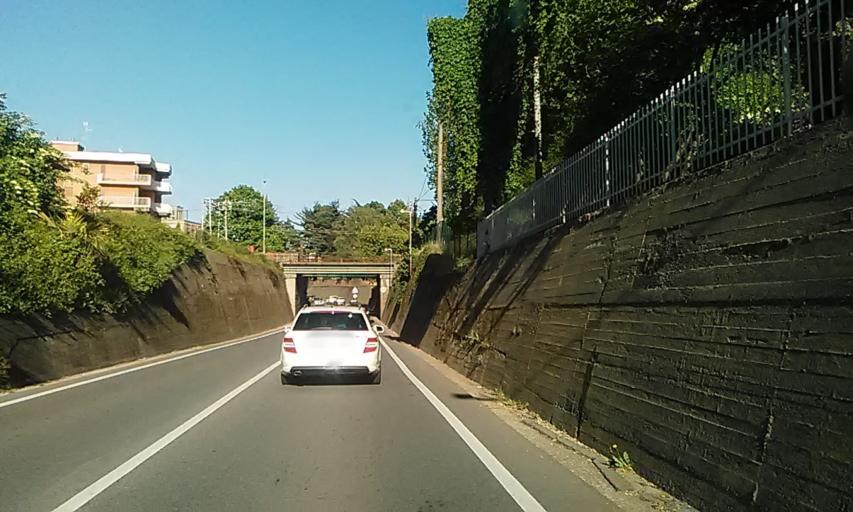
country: IT
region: Piedmont
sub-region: Provincia di Novara
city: Oleggio
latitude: 45.5949
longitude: 8.6316
